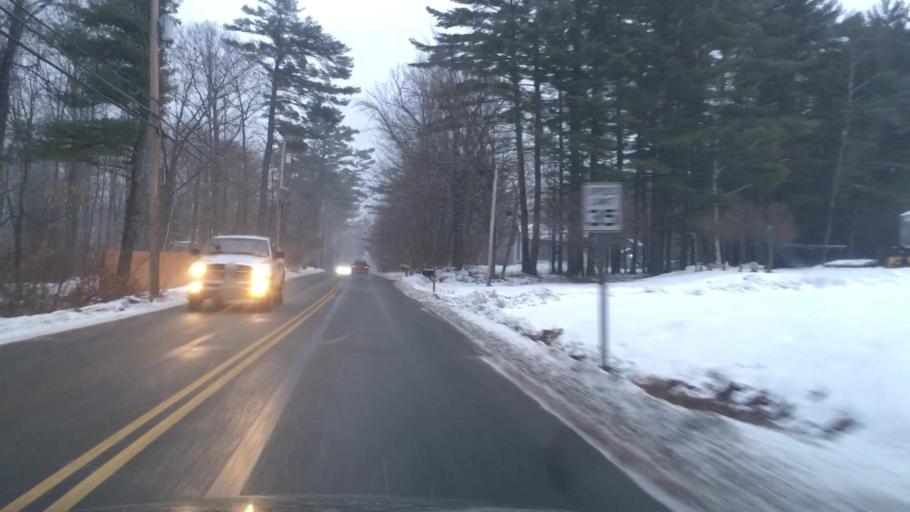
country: US
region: New Hampshire
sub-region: Sullivan County
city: Newport
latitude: 43.3616
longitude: -72.1601
